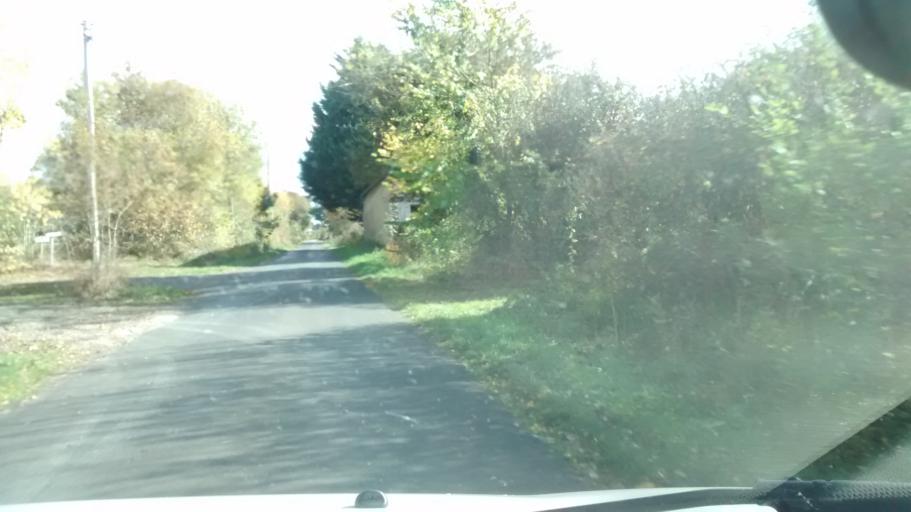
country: FR
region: Pays de la Loire
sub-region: Departement de Maine-et-Loire
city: Feneu
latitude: 47.5622
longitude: -0.5790
